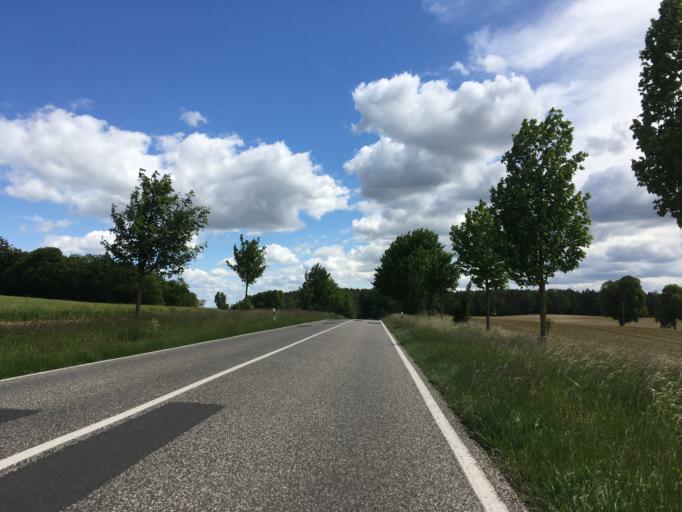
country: DE
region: Brandenburg
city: Protzel
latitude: 52.7083
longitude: 14.0120
